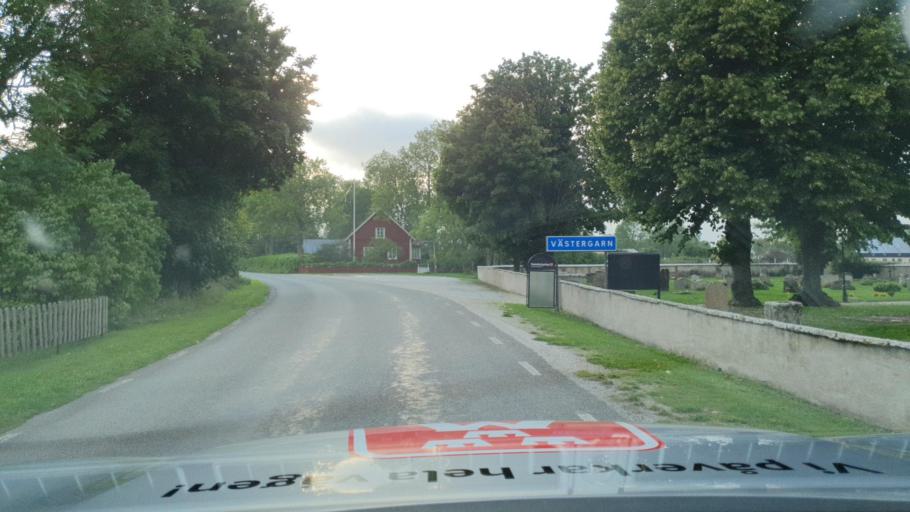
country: SE
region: Gotland
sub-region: Gotland
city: Klintehamn
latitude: 57.4406
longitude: 18.1513
